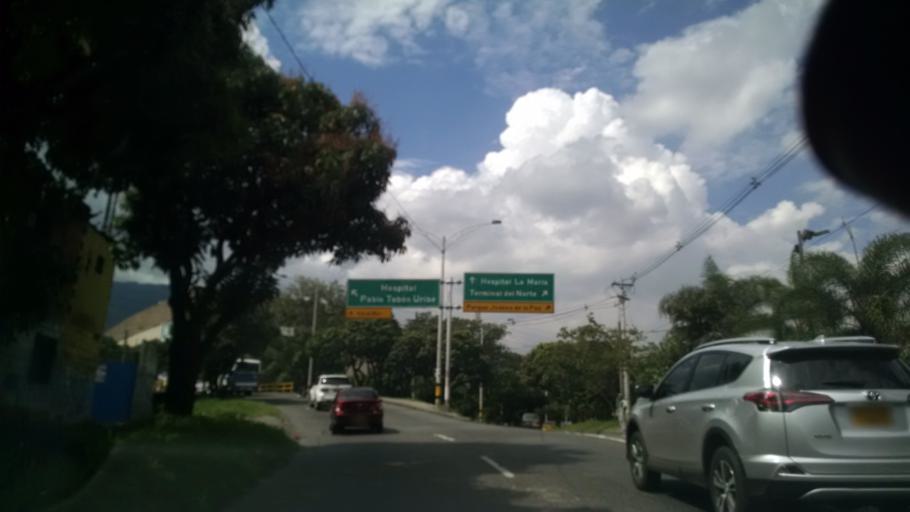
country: CO
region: Antioquia
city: Medellin
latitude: 6.2691
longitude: -75.5757
